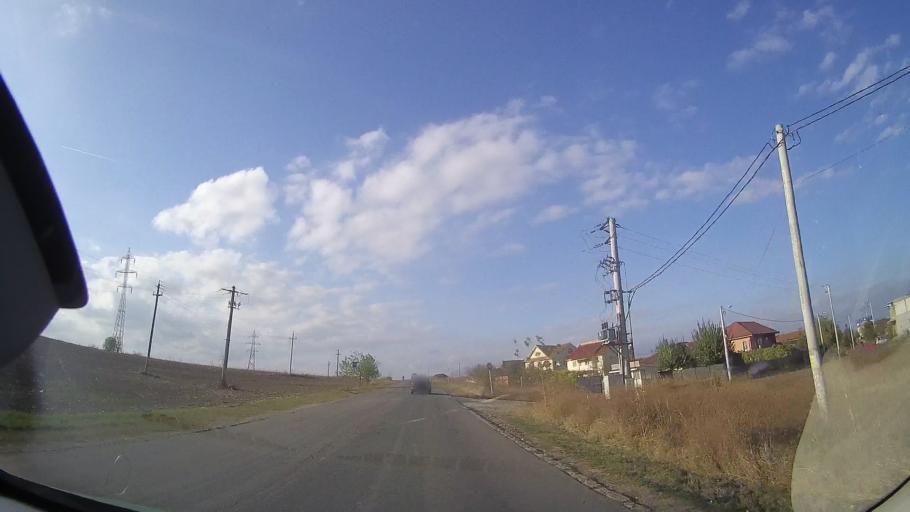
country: RO
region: Constanta
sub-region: Comuna Limanu
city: Limanu
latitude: 43.7923
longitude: 28.5462
